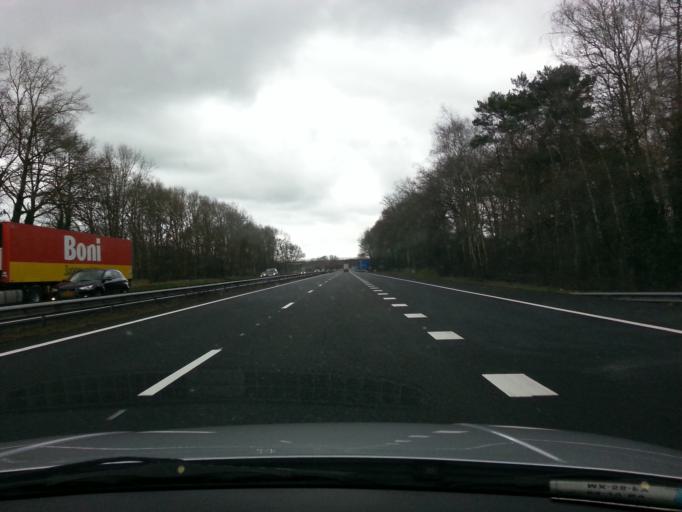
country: NL
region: Gelderland
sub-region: Gemeente Oldebroek
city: Oldebroek
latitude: 52.4549
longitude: 5.9789
